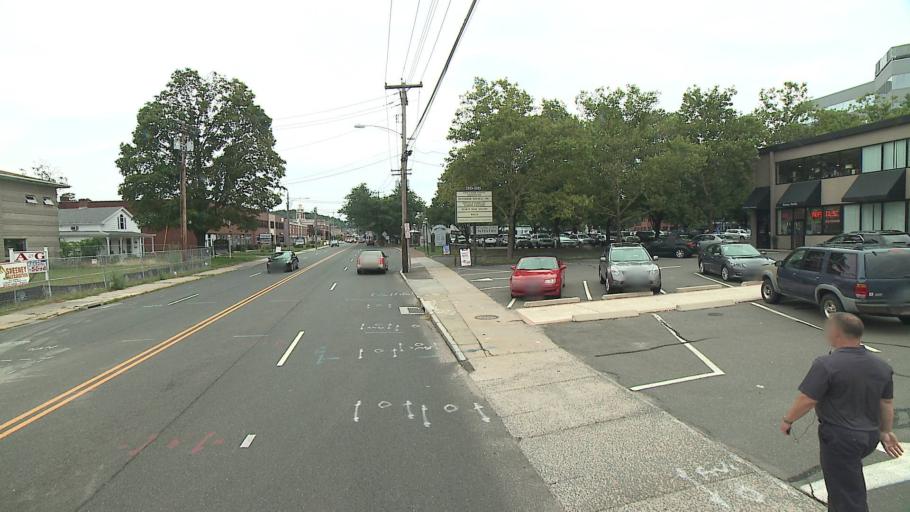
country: US
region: Connecticut
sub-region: New Haven County
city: Hamden
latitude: 41.3816
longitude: -72.9025
